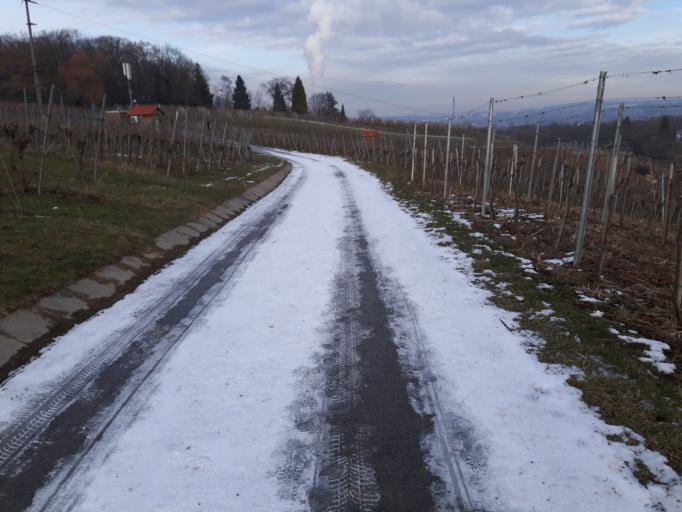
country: DE
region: Baden-Wuerttemberg
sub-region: Regierungsbezirk Stuttgart
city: Besigheim
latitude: 49.0047
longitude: 9.1354
